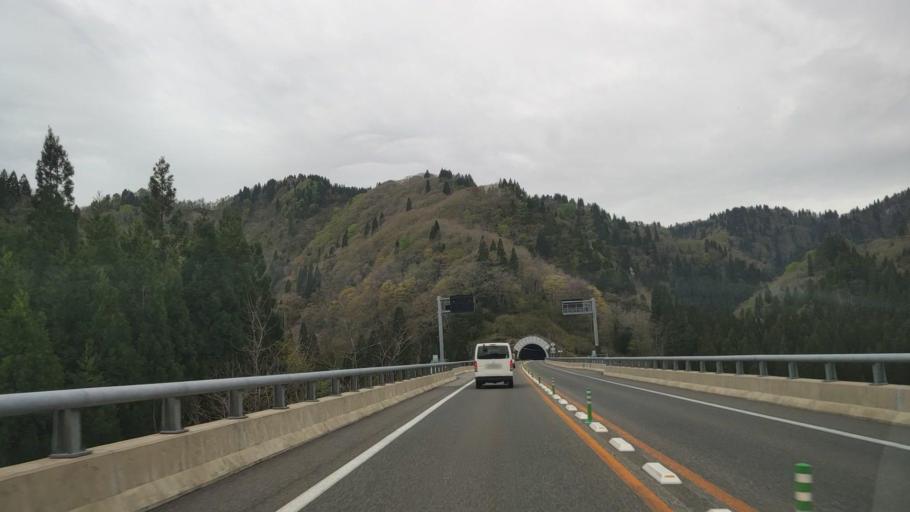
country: JP
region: Akita
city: Odate
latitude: 40.3443
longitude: 140.6601
